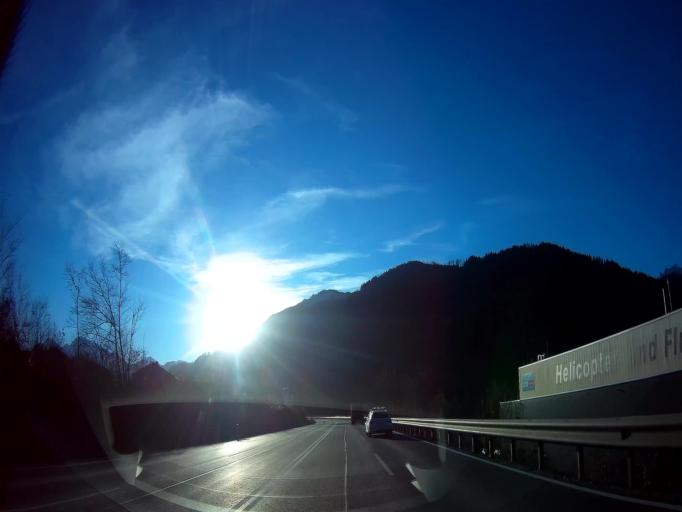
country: AT
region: Salzburg
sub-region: Politischer Bezirk Sankt Johann im Pongau
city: Bischofshofen
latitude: 47.3936
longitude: 13.2258
